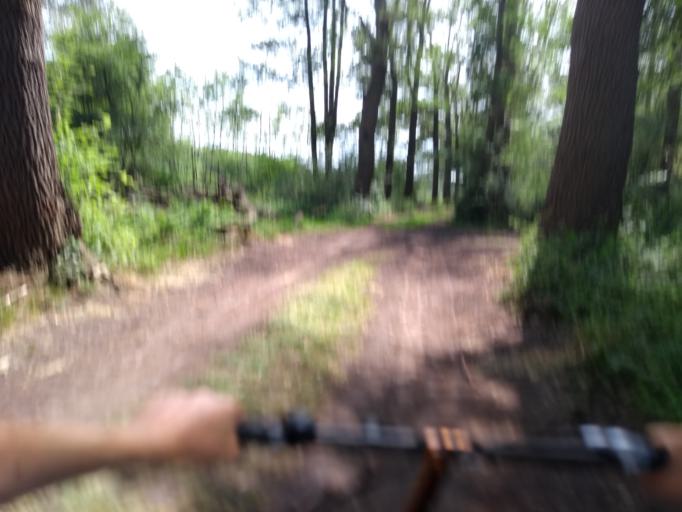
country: NL
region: Overijssel
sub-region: Gemeente Almelo
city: Almelo
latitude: 52.3637
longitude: 6.7095
